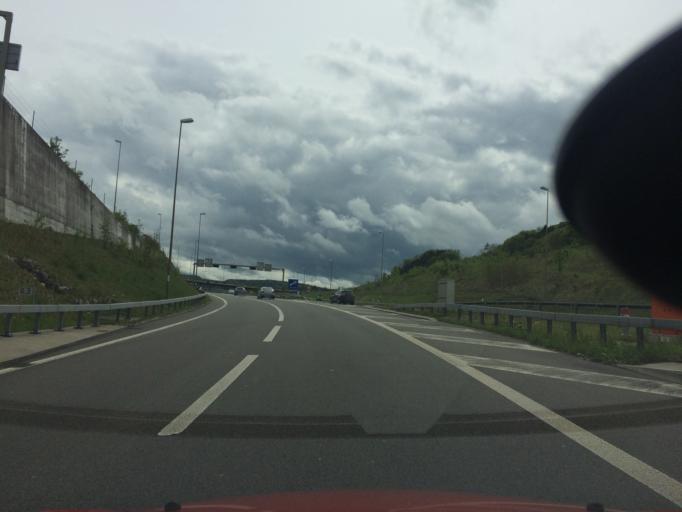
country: CH
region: Zurich
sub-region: Bezirk Affoltern
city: Wettswil / Wettswil (Dorf)
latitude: 47.3418
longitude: 8.4580
